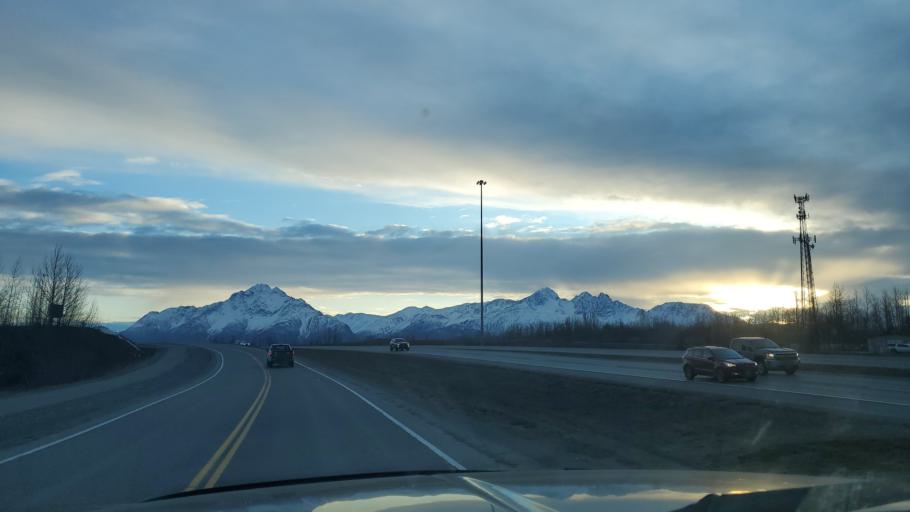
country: US
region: Alaska
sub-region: Matanuska-Susitna Borough
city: Lakes
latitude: 61.5648
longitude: -149.3046
